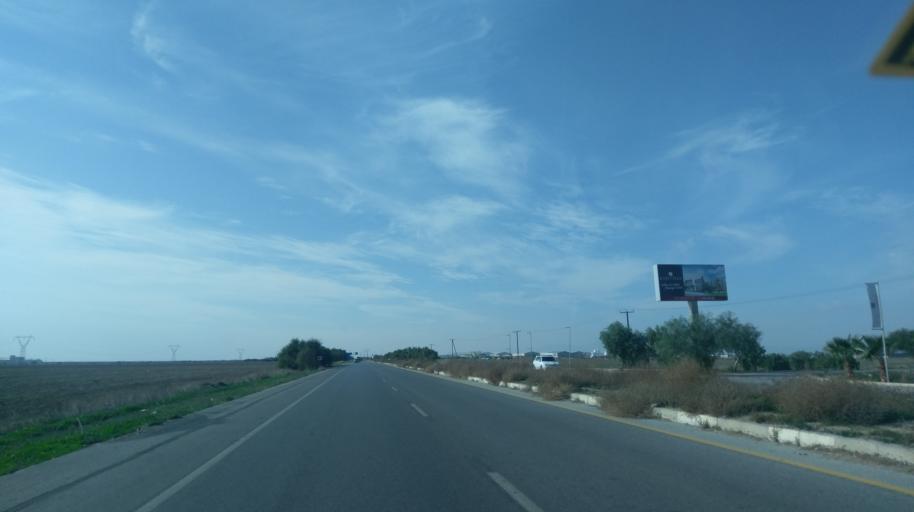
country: CY
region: Ammochostos
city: Acheritou
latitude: 35.1375
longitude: 33.8820
